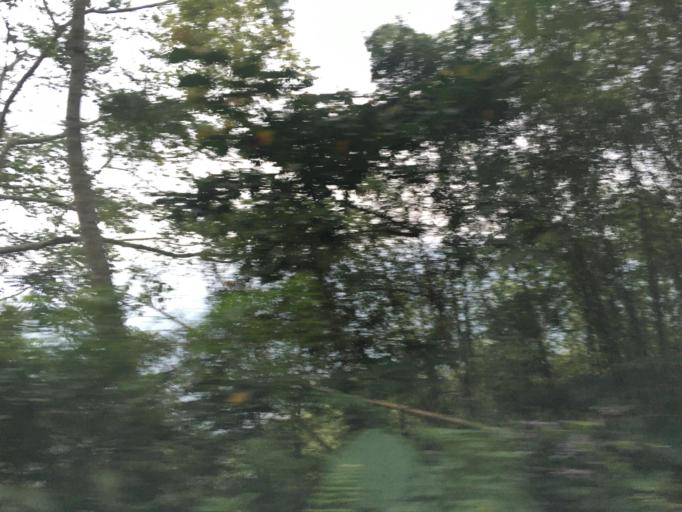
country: TW
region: Taiwan
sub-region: Chiayi
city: Jiayi Shi
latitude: 23.5359
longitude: 120.6334
